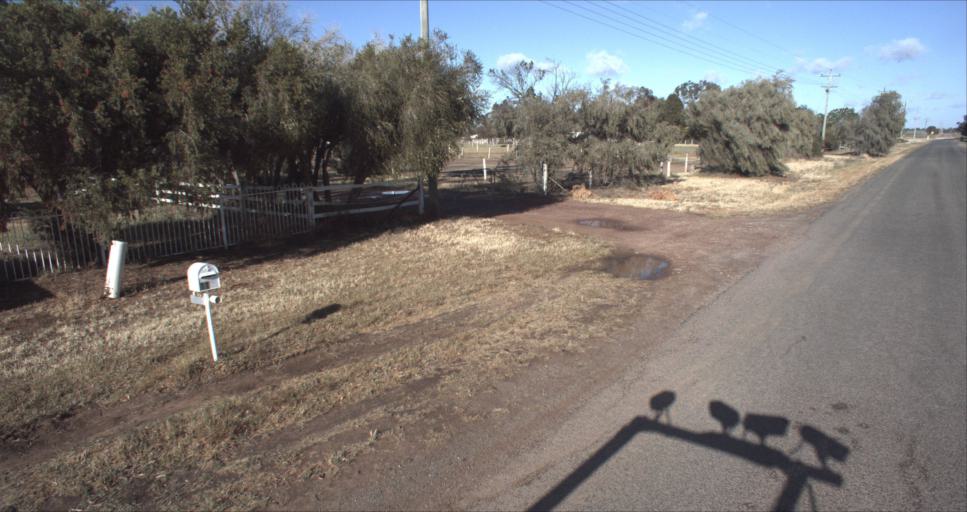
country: AU
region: New South Wales
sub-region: Leeton
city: Leeton
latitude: -34.5384
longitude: 146.3868
